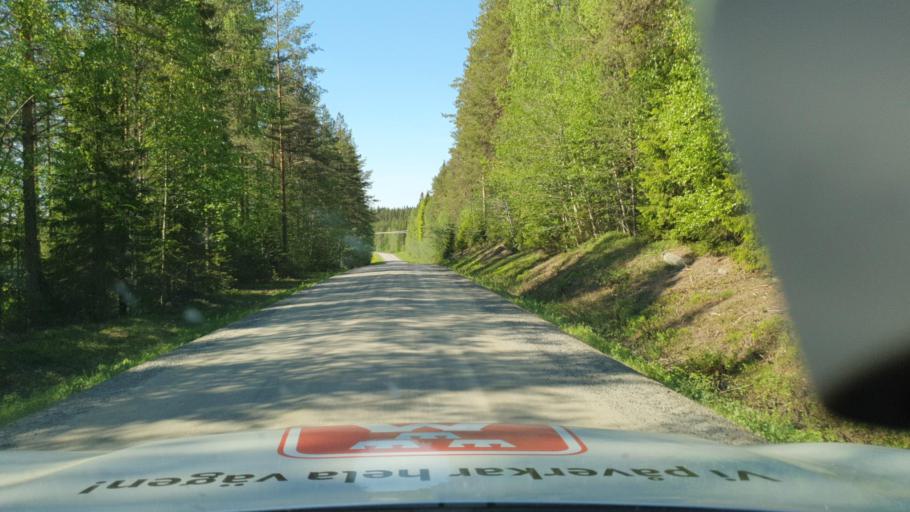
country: SE
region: Vaesterbotten
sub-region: Vannas Kommun
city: Vaennaes
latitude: 64.0084
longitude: 19.7324
